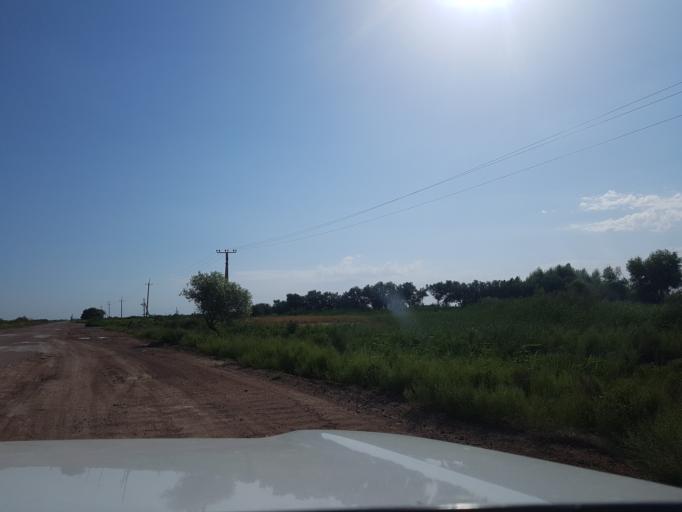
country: TM
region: Dasoguz
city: Koeneuergench
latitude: 42.0454
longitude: 58.8231
